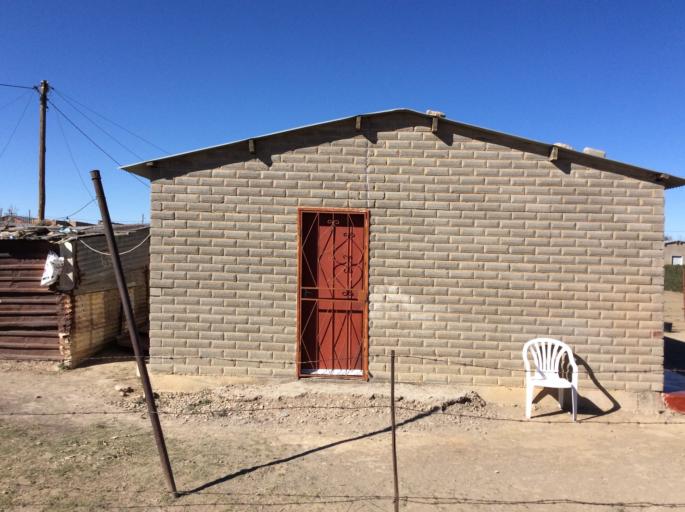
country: ZA
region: Orange Free State
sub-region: Lejweleputswa District Municipality
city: Brandfort
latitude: -28.7346
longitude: 26.1055
